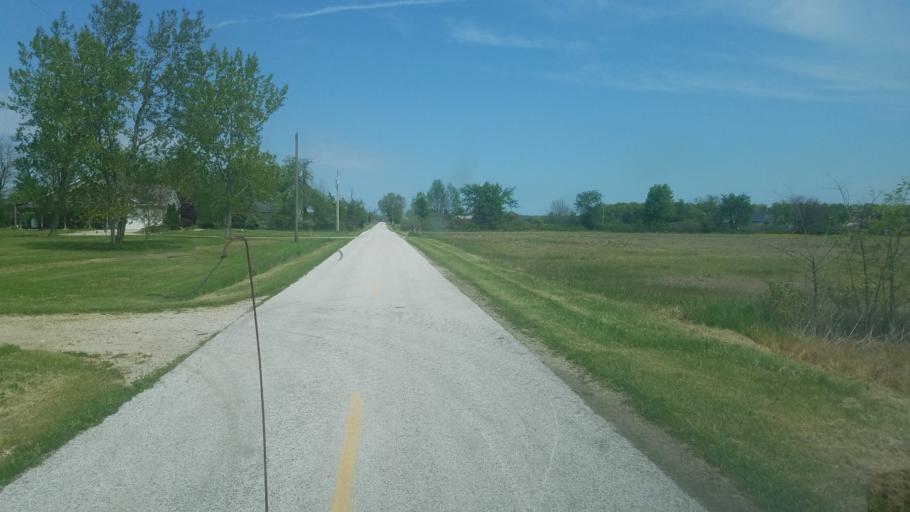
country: US
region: Ohio
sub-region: Ottawa County
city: Oak Harbor
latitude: 41.4797
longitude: -83.2019
